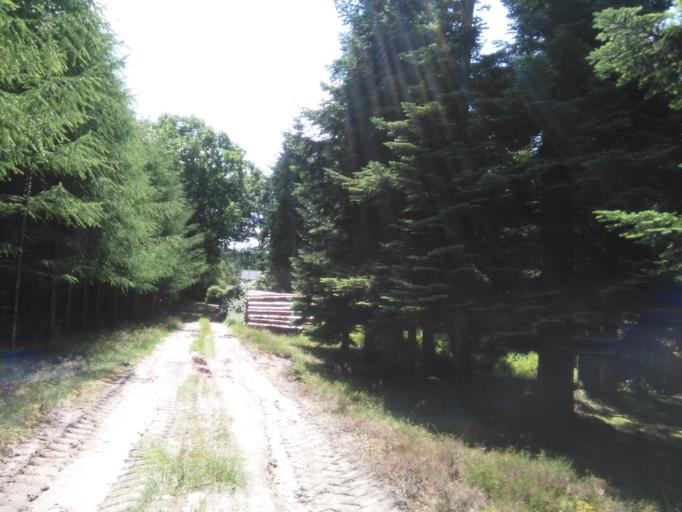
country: DK
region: Central Jutland
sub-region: Silkeborg Kommune
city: Virklund
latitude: 56.0662
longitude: 9.4601
